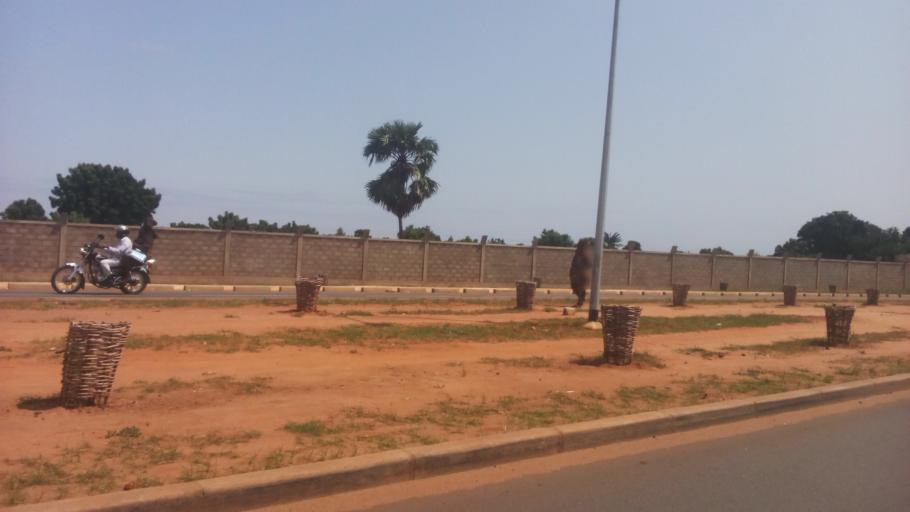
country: TG
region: Maritime
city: Lome
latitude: 6.1877
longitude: 1.2617
